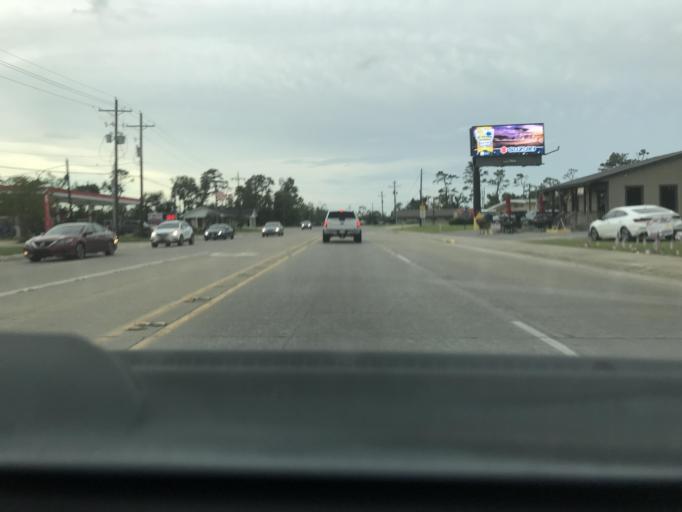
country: US
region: Louisiana
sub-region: Calcasieu Parish
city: Westlake
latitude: 30.2644
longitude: -93.2581
